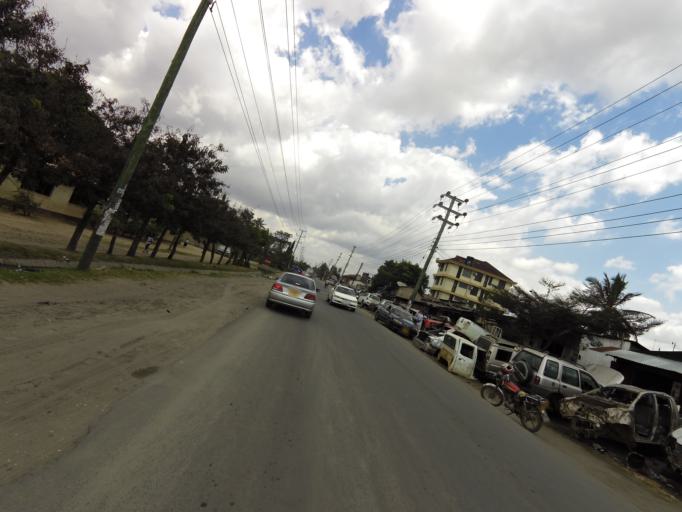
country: TZ
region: Dar es Salaam
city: Magomeni
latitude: -6.7910
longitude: 39.2365
